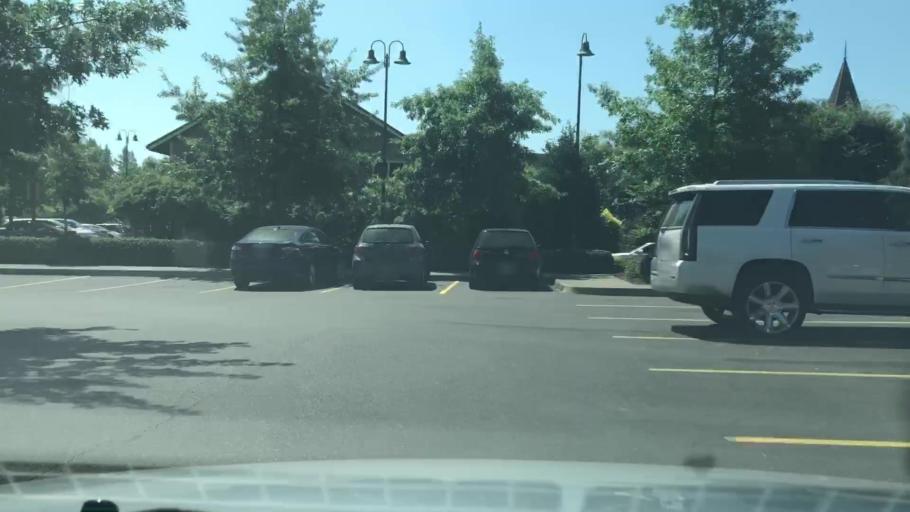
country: US
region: Oregon
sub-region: Clackamas County
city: Wilsonville
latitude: 45.3012
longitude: -122.7726
